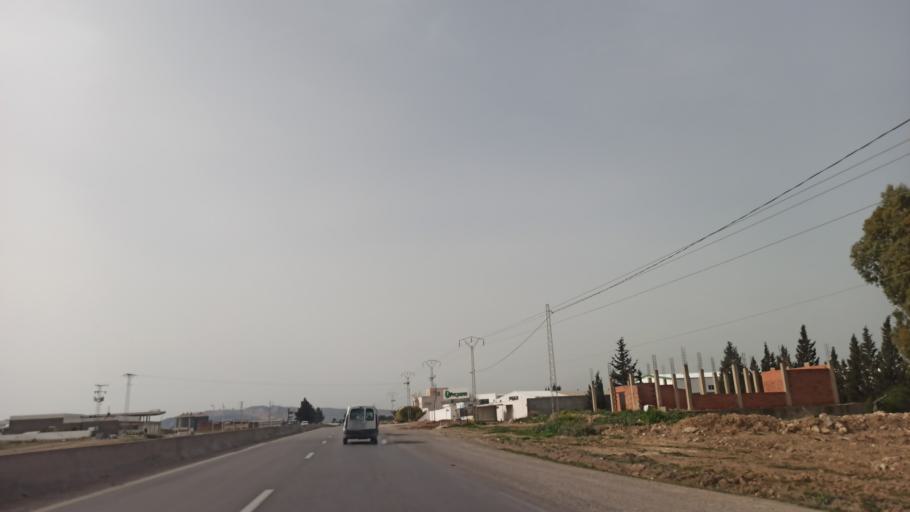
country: TN
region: Tunis
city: La Mohammedia
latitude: 36.5854
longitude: 10.0996
